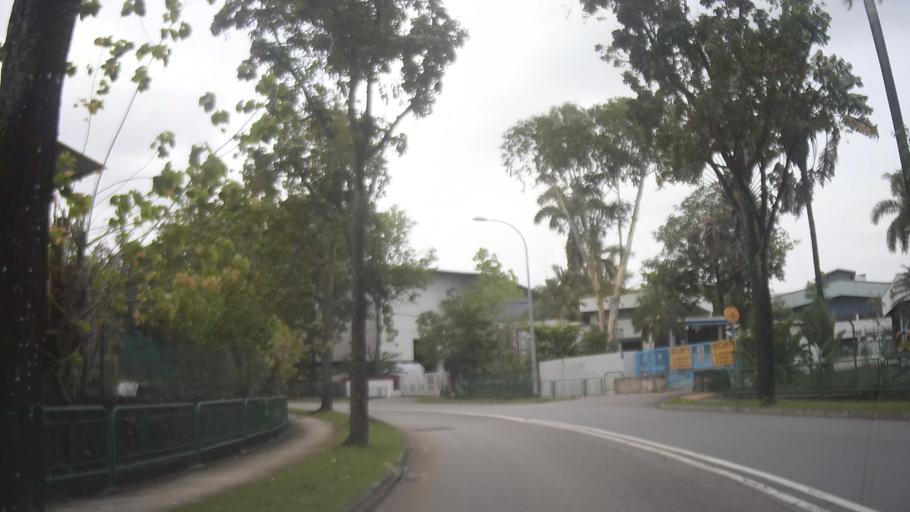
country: MY
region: Johor
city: Johor Bahru
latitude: 1.4094
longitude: 103.7484
